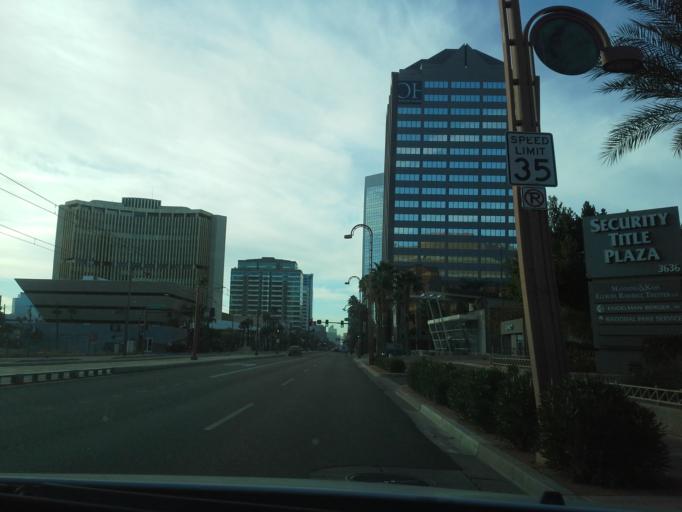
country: US
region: Arizona
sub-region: Maricopa County
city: Phoenix
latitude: 33.4907
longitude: -112.0740
